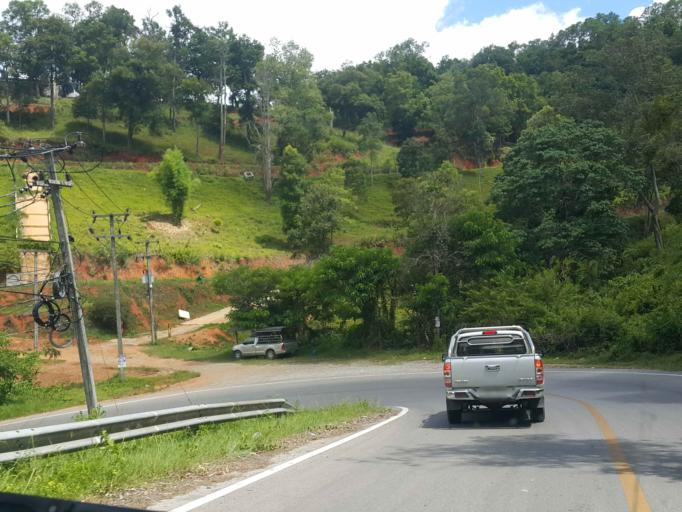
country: TH
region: Chiang Mai
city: Samoeng
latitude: 18.8789
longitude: 98.8093
